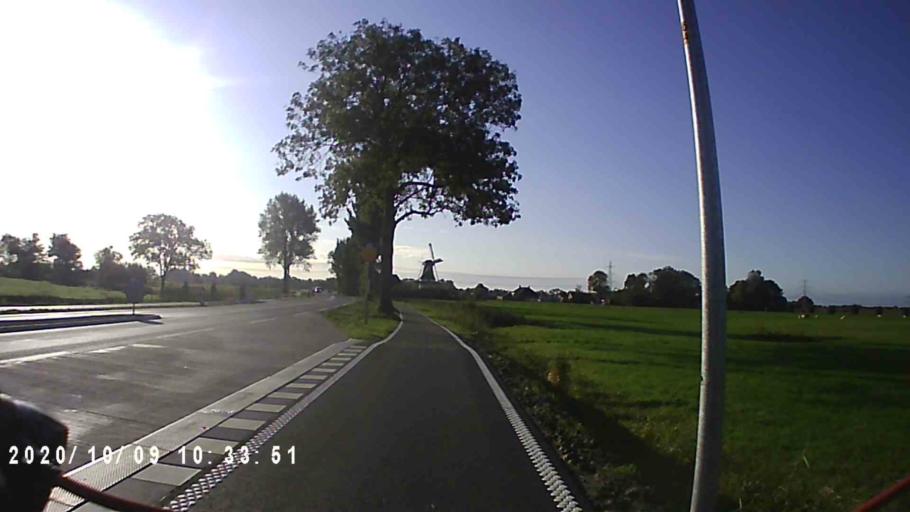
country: NL
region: Groningen
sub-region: Gemeente Winsum
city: Winsum
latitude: 53.3035
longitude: 6.5318
